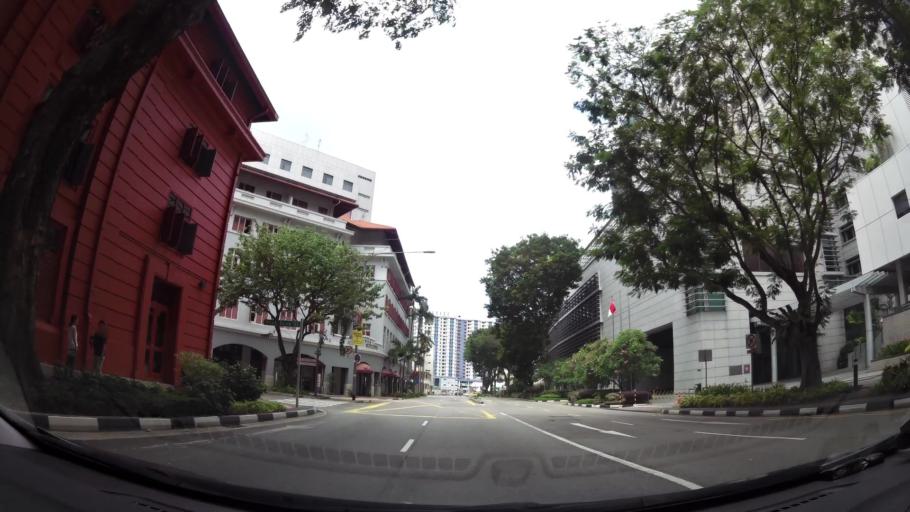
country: SG
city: Singapore
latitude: 1.2790
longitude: 103.8457
